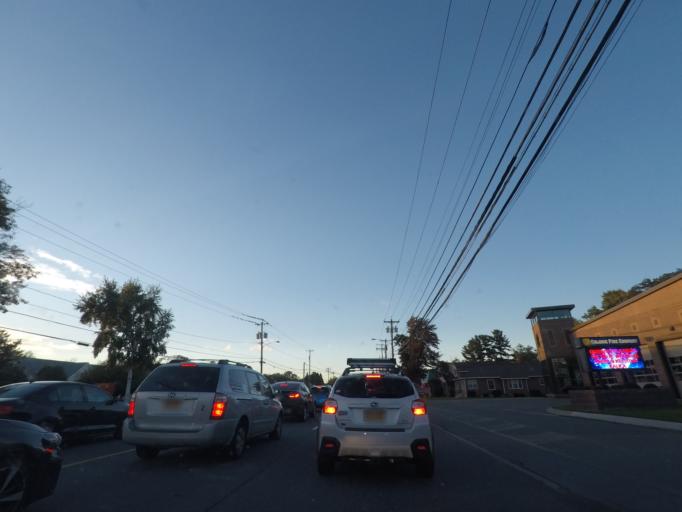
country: US
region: New York
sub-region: Albany County
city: Colonie
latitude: 42.7193
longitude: -73.8347
